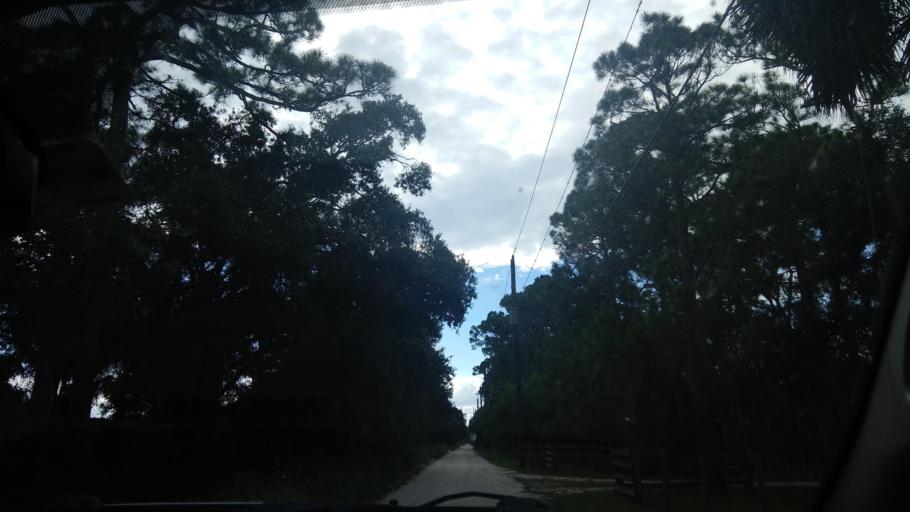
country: US
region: Florida
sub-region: Indian River County
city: Fellsmere
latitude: 27.7865
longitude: -80.6030
